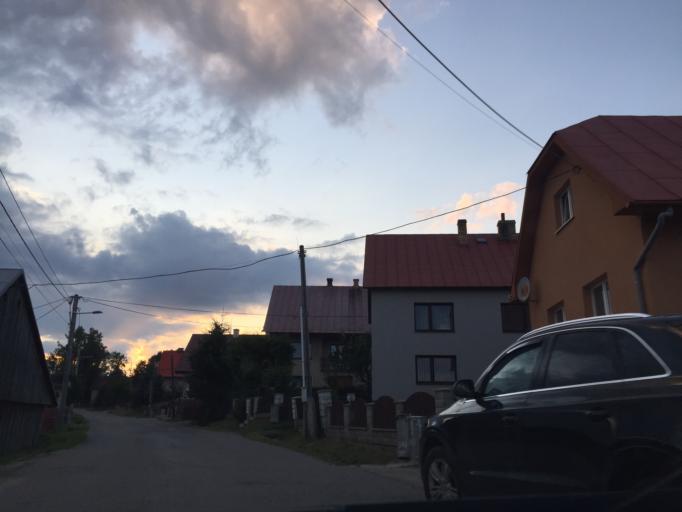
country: PL
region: Silesian Voivodeship
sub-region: Powiat zywiecki
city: Sopotnia Wielka
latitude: 49.4681
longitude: 19.3098
